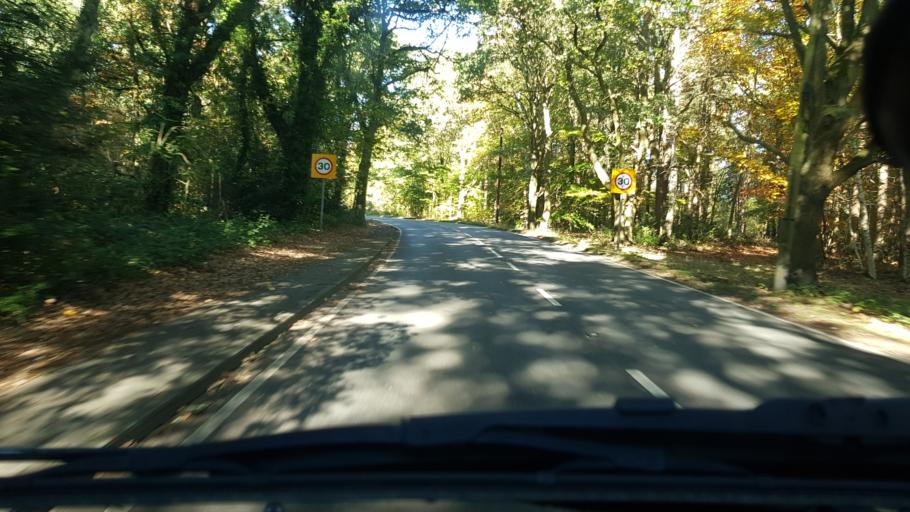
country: GB
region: England
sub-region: Surrey
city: Pirbright
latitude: 51.2875
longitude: -0.6432
